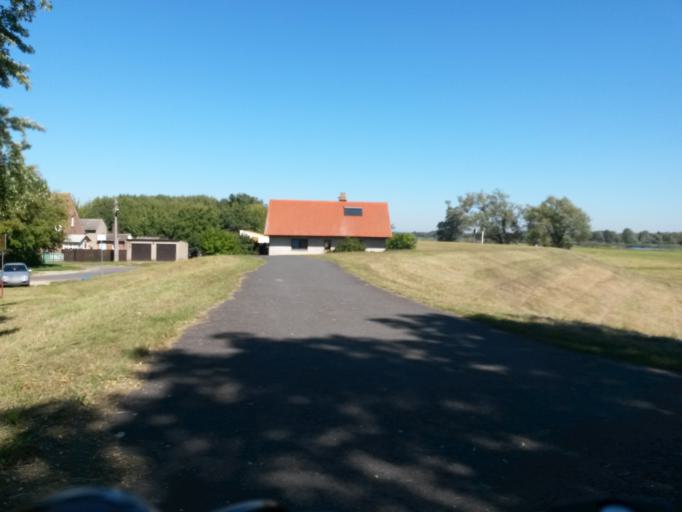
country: PL
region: West Pomeranian Voivodeship
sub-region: Powiat gryfinski
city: Cedynia
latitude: 52.8649
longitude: 14.1407
